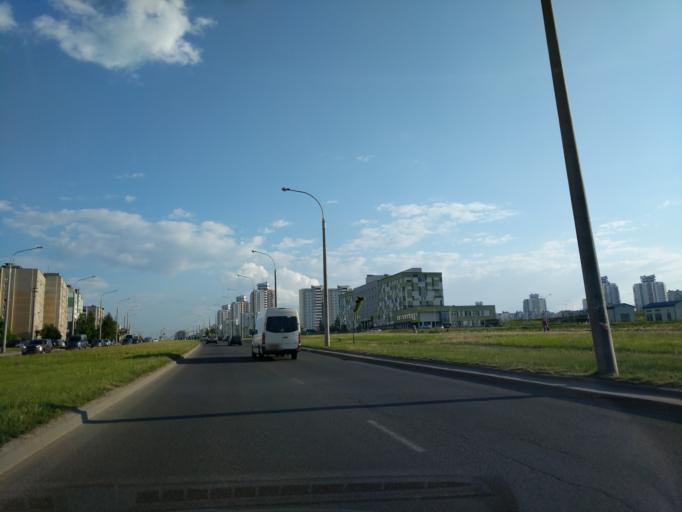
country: BY
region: Minsk
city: Zhdanovichy
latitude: 53.9197
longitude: 27.4374
